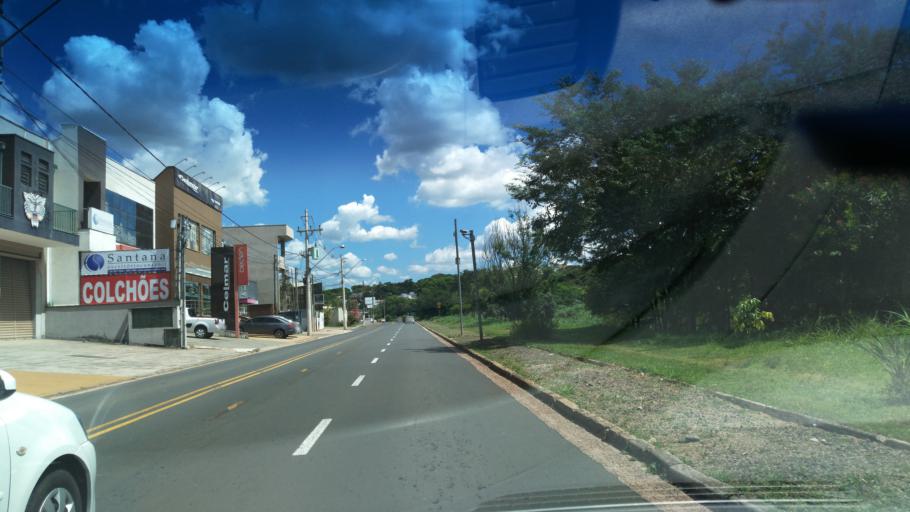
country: BR
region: Sao Paulo
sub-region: Valinhos
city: Valinhos
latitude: -22.9692
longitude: -47.0121
